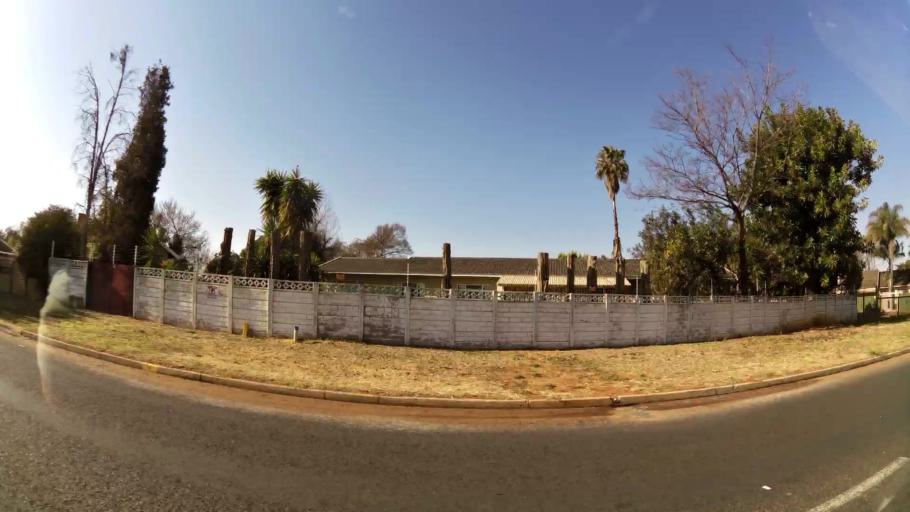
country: ZA
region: Gauteng
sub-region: City of Johannesburg Metropolitan Municipality
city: Modderfontein
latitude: -26.0550
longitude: 28.2046
